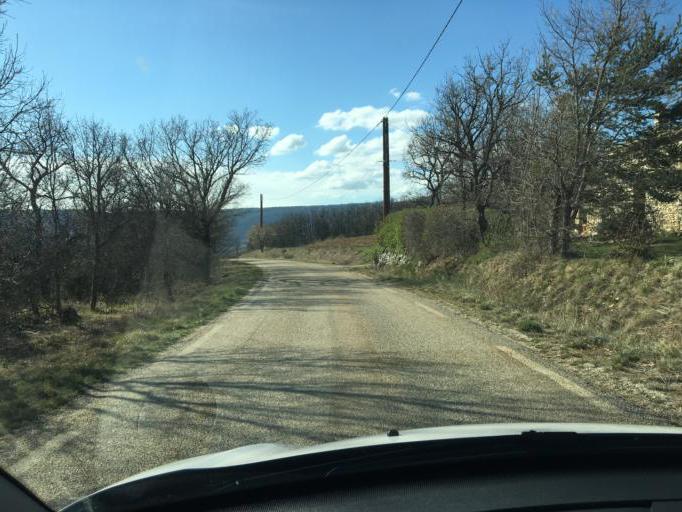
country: FR
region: Provence-Alpes-Cote d'Azur
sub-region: Departement du Vaucluse
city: Sault
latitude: 44.0823
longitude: 5.4142
